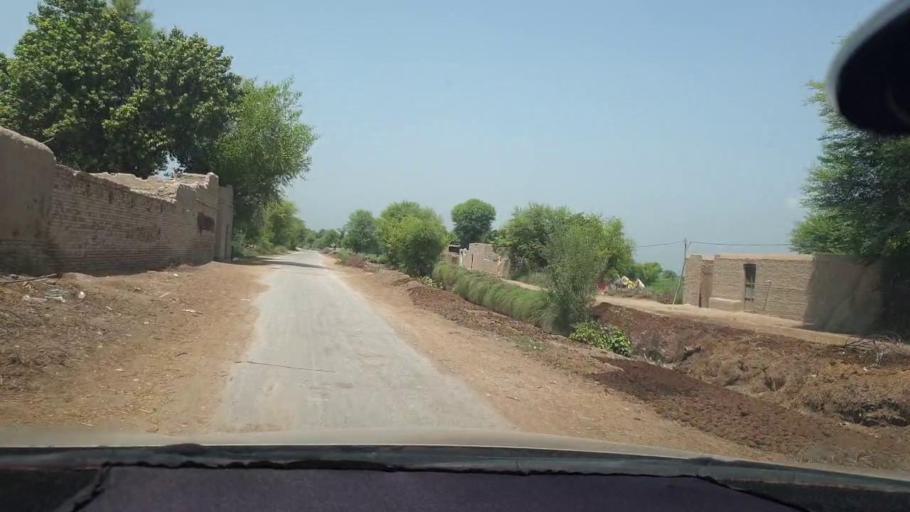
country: PK
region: Sindh
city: Kambar
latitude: 27.6506
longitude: 67.9664
